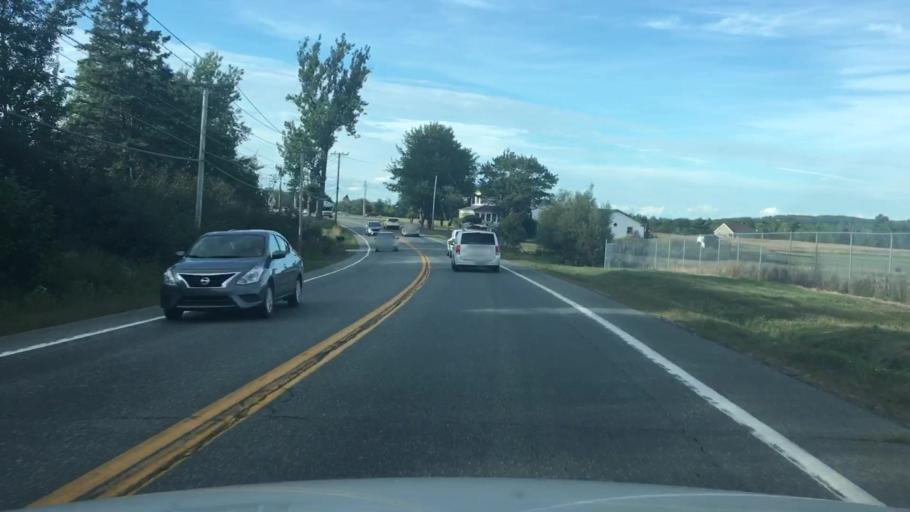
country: US
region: Maine
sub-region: Hancock County
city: Trenton
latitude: 44.4585
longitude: -68.3613
